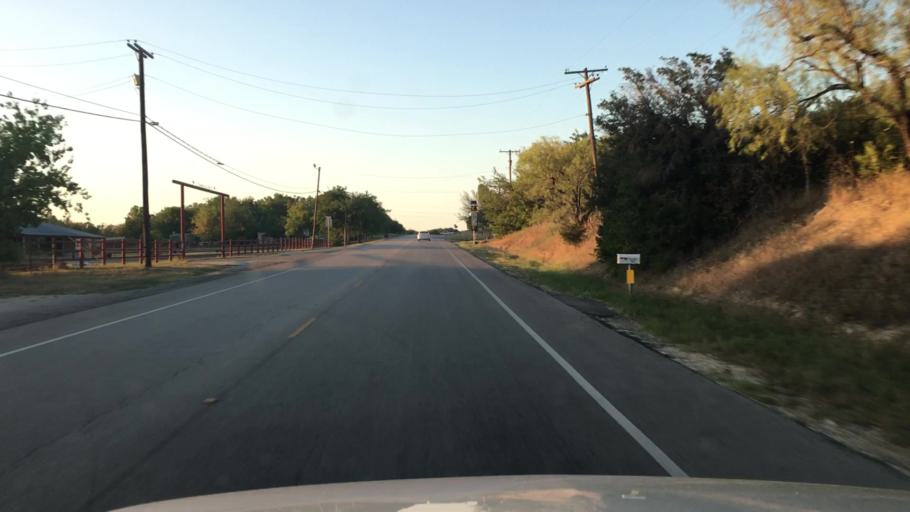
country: US
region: Texas
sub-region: Hamilton County
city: Hico
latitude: 31.9897
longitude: -98.0266
